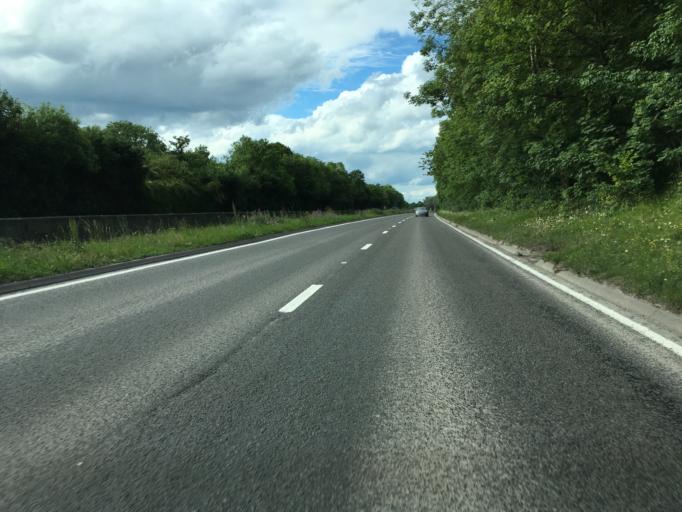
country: GB
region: England
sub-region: Oxfordshire
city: Cowley
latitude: 51.7536
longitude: -1.1951
